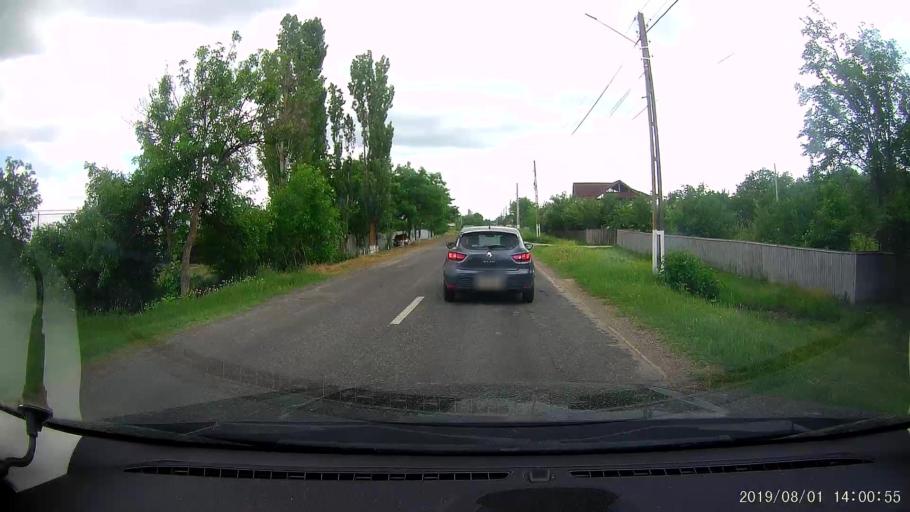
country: RO
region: Galati
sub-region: Comuna Foltesti
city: Foltesti
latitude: 45.7564
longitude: 28.0736
